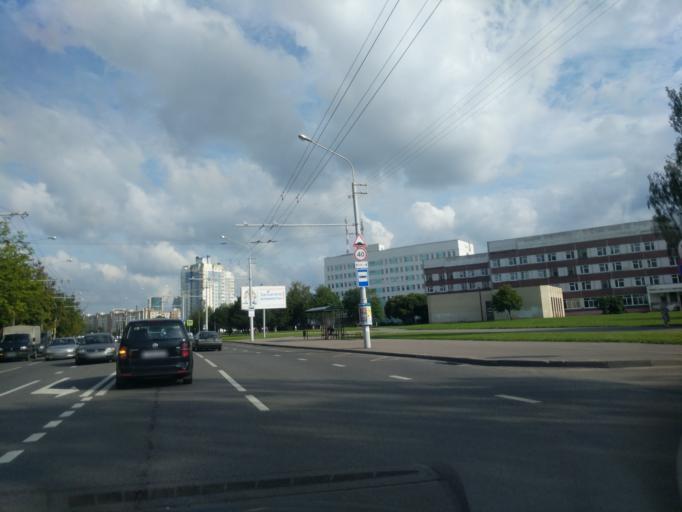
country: BY
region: Minsk
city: Novoye Medvezhino
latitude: 53.8675
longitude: 27.4646
